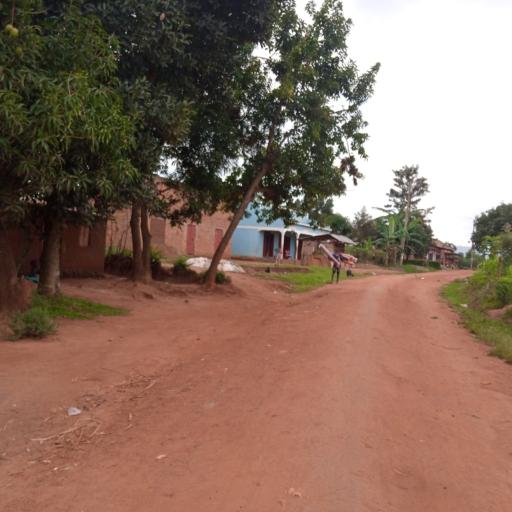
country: UG
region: Eastern Region
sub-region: Mbale District
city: Mbale
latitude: 1.1187
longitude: 34.1768
